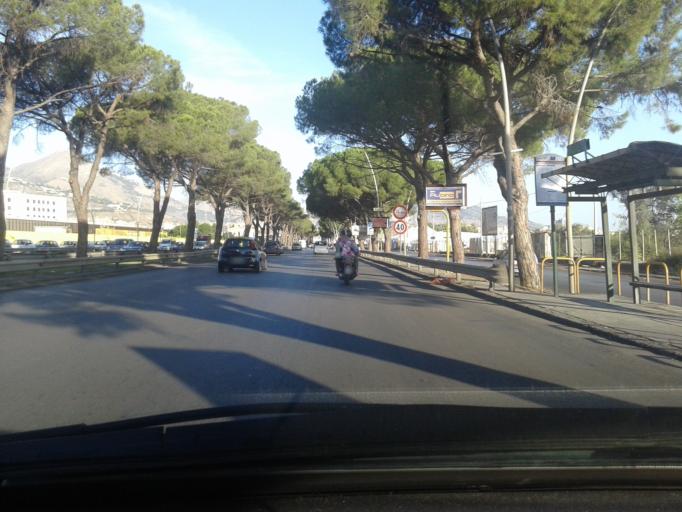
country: IT
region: Sicily
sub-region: Palermo
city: Villa Ciambra
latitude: 38.0909
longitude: 13.3433
